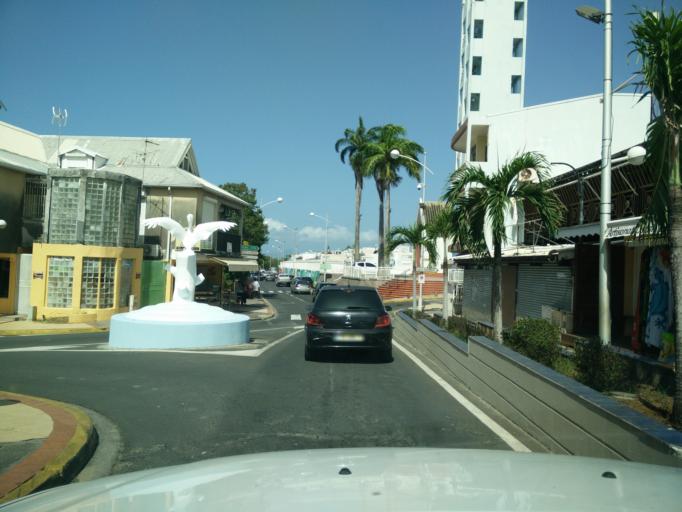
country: GP
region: Guadeloupe
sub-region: Guadeloupe
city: Le Gosier
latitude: 16.2064
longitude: -61.4939
